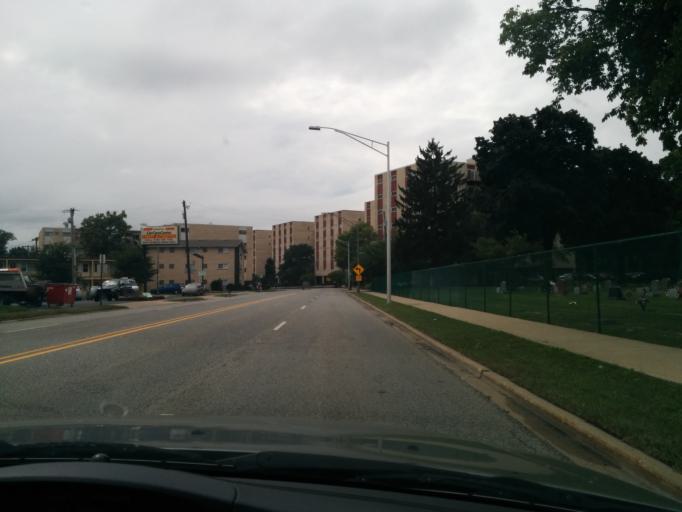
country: US
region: Illinois
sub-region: Cook County
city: Forest Park
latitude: 41.8693
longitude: -87.8180
